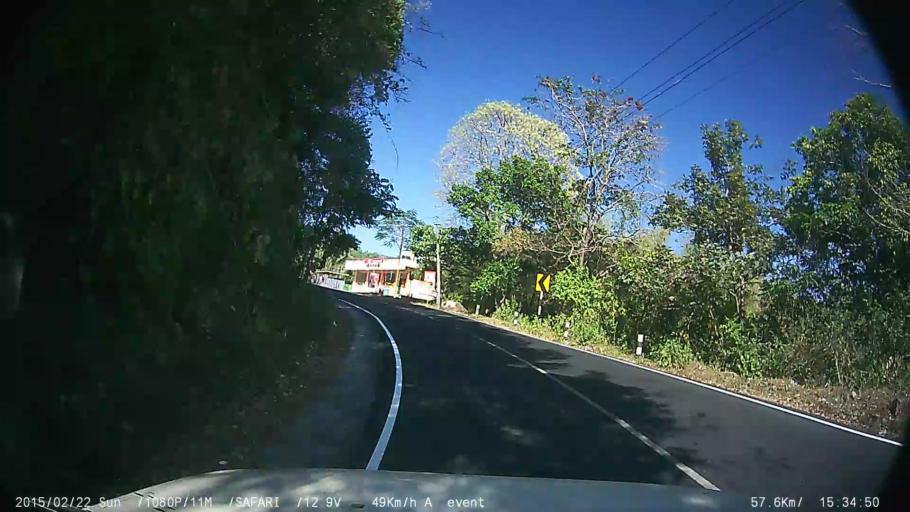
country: IN
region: Kerala
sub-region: Kottayam
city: Erattupetta
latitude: 9.5542
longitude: 76.9738
